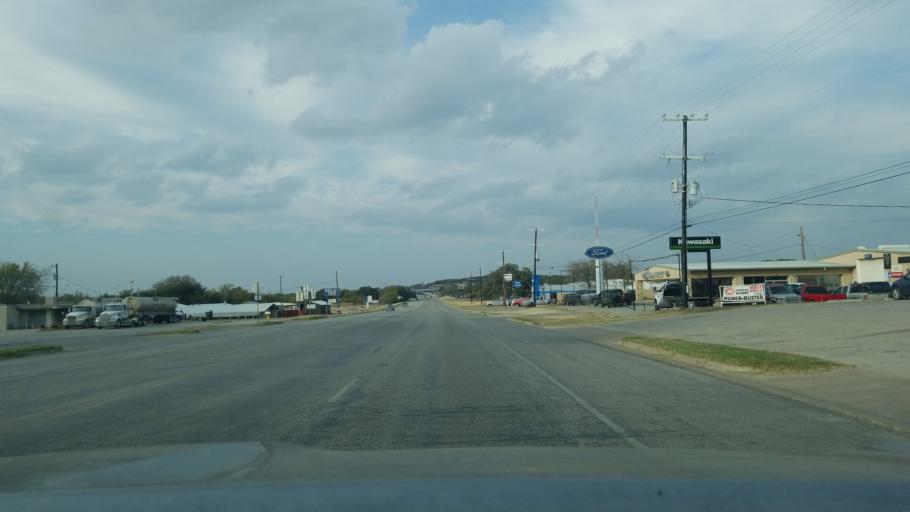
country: US
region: Texas
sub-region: Mills County
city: Goldthwaite
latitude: 31.4695
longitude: -98.5681
